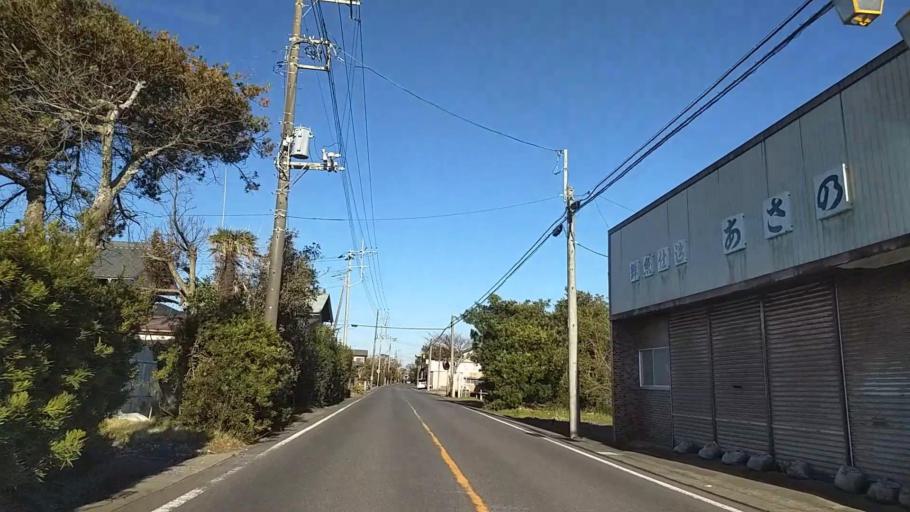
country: JP
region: Chiba
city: Naruto
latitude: 35.5882
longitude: 140.4991
